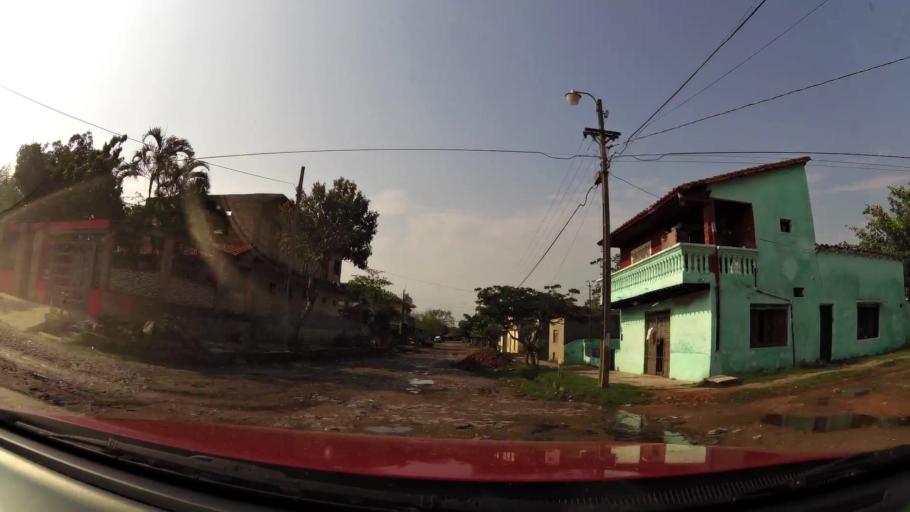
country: PY
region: Presidente Hayes
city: Nanawa
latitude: -25.2973
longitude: -57.6664
